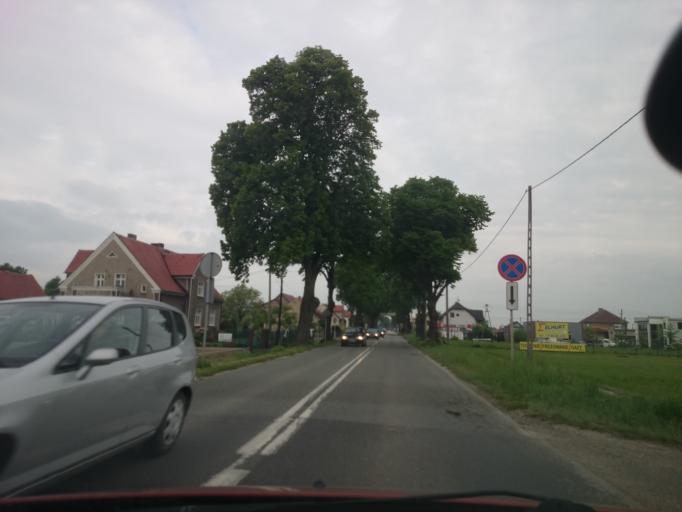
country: PL
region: Opole Voivodeship
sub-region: Powiat opolski
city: Dobrzen Wielki
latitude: 50.7454
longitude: 17.8693
